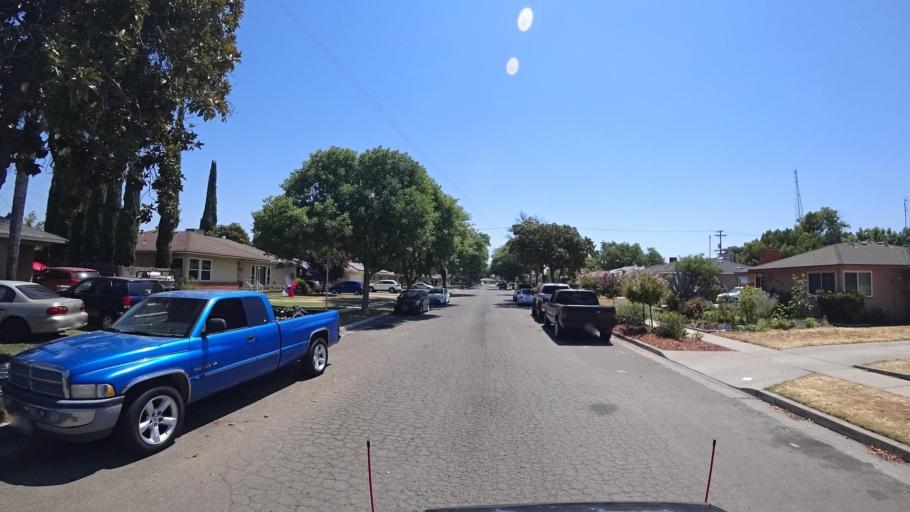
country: US
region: California
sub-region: Fresno County
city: Fresno
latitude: 36.7732
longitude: -119.7757
